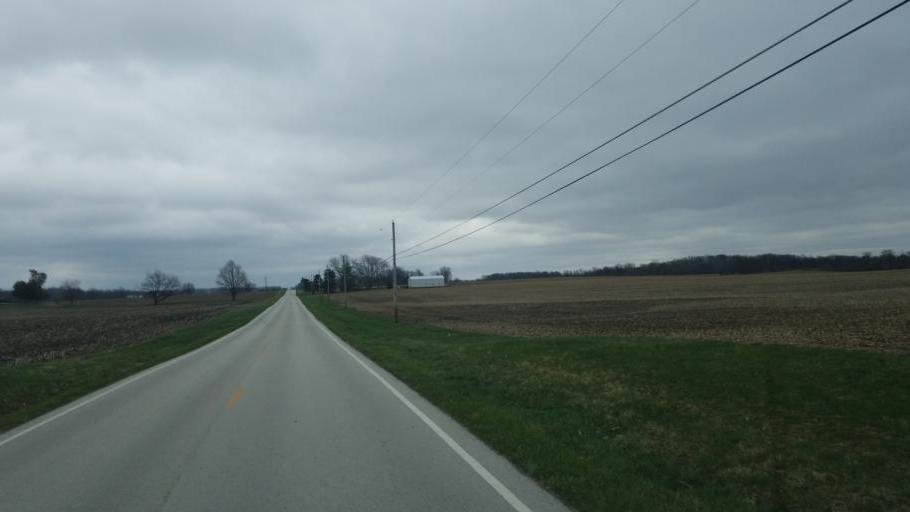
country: US
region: Ohio
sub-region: Wyandot County
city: Upper Sandusky
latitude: 40.8258
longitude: -83.2178
